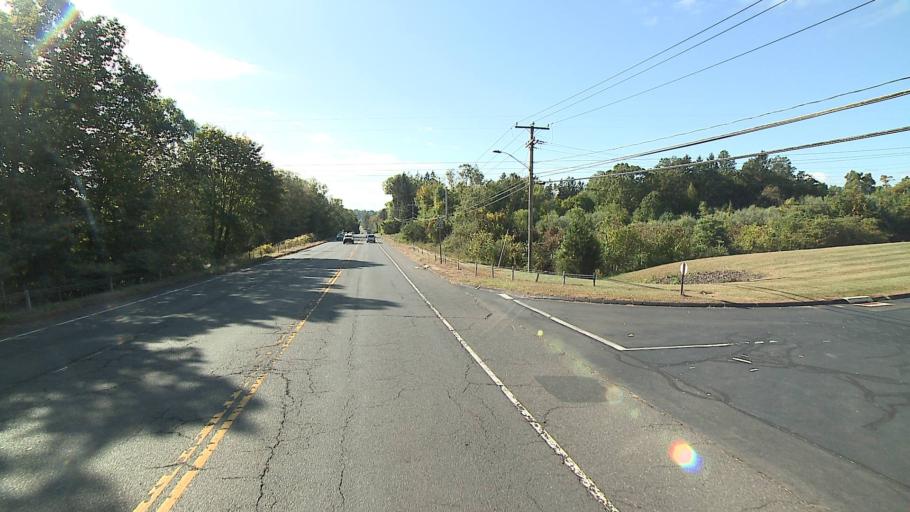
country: US
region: Connecticut
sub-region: Hartford County
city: Plainville
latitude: 41.6250
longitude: -72.8998
